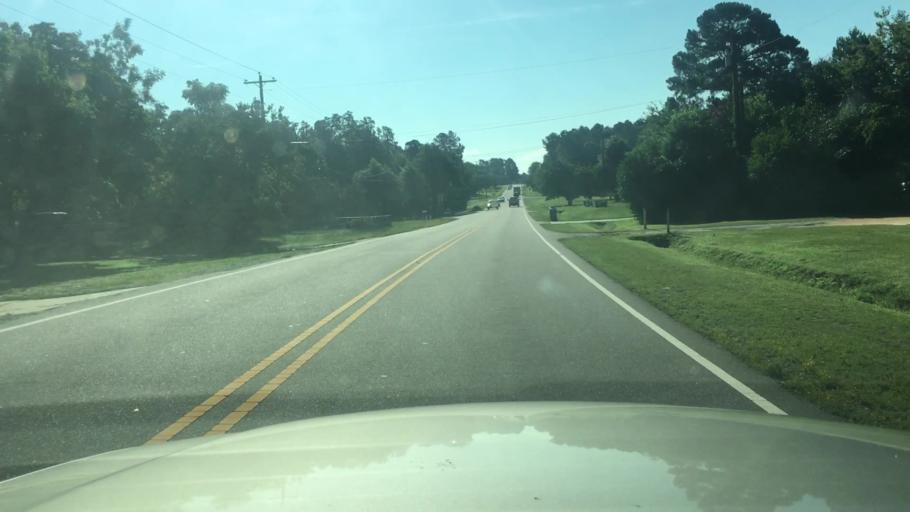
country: US
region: North Carolina
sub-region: Cumberland County
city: Fayetteville
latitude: 35.1334
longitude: -78.8903
